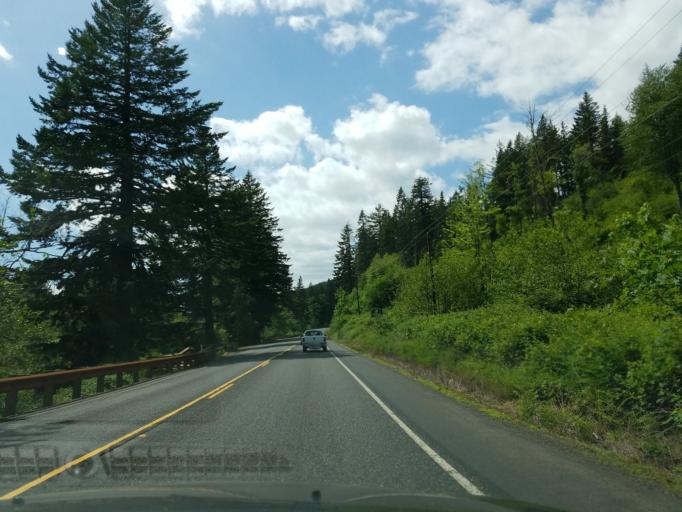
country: US
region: Oregon
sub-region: Hood River County
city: Cascade Locks
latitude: 45.6070
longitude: -122.0797
